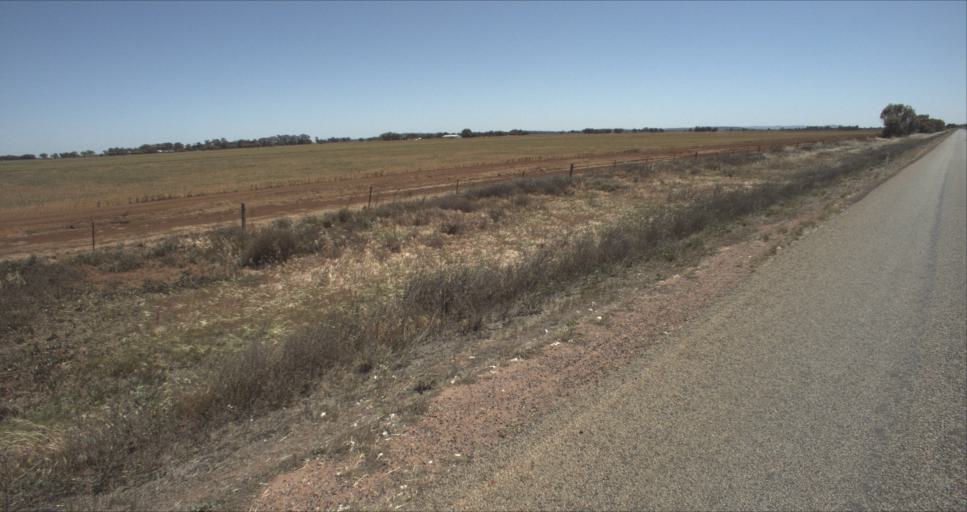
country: AU
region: New South Wales
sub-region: Leeton
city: Leeton
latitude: -34.4644
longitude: 146.2935
